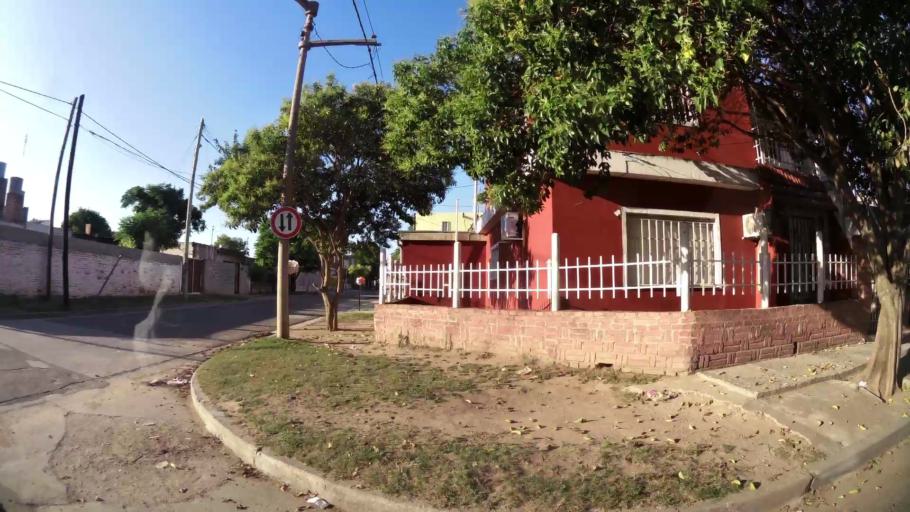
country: AR
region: Cordoba
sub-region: Departamento de Capital
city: Cordoba
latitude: -31.3751
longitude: -64.1922
